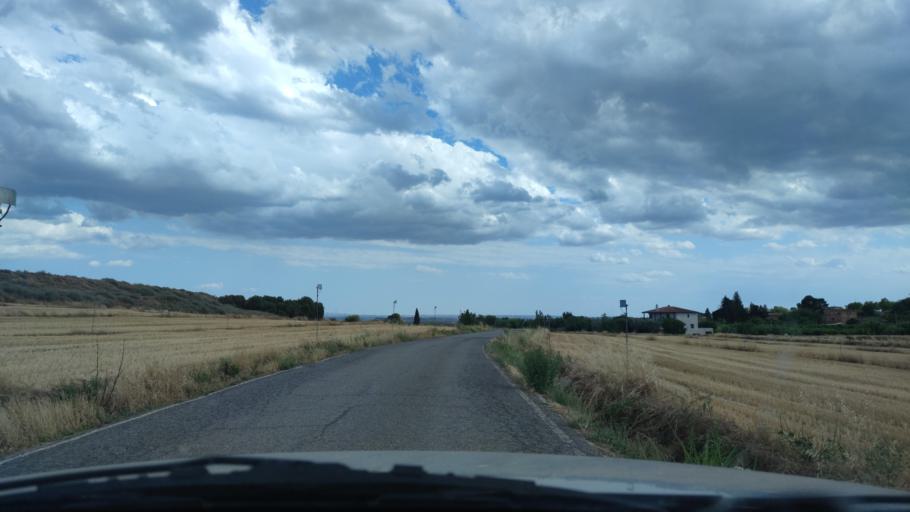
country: ES
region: Catalonia
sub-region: Provincia de Lleida
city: Lleida
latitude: 41.6055
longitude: 0.5852
